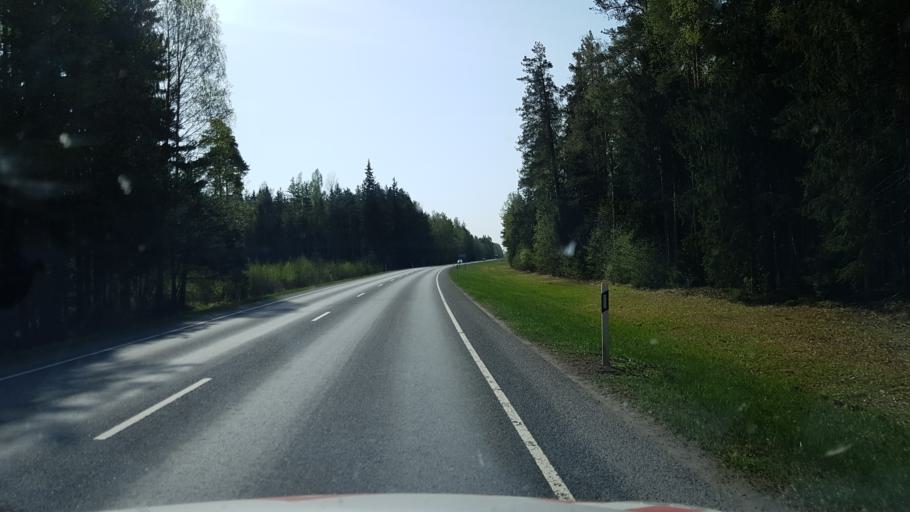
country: EE
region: Paernumaa
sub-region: Paikuse vald
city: Paikuse
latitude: 58.2524
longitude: 24.6836
